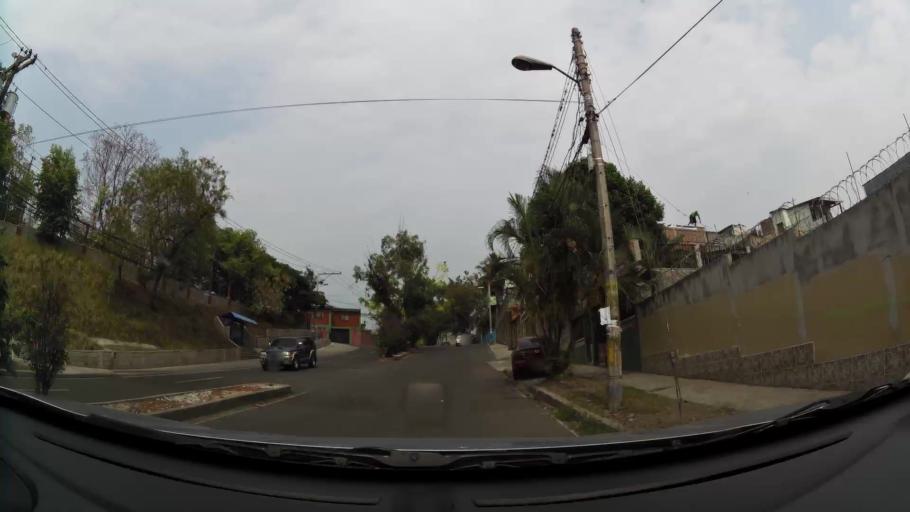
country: HN
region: Francisco Morazan
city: Tegucigalpa
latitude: 14.0741
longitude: -87.1867
